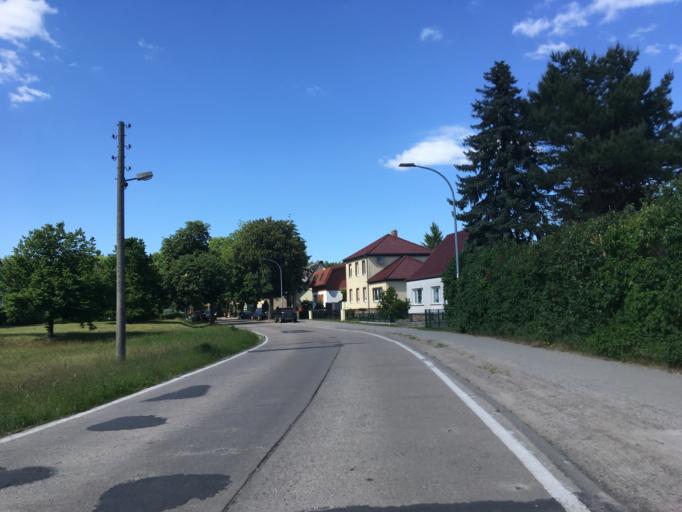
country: DE
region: Brandenburg
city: Joachimsthal
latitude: 52.9865
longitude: 13.7437
